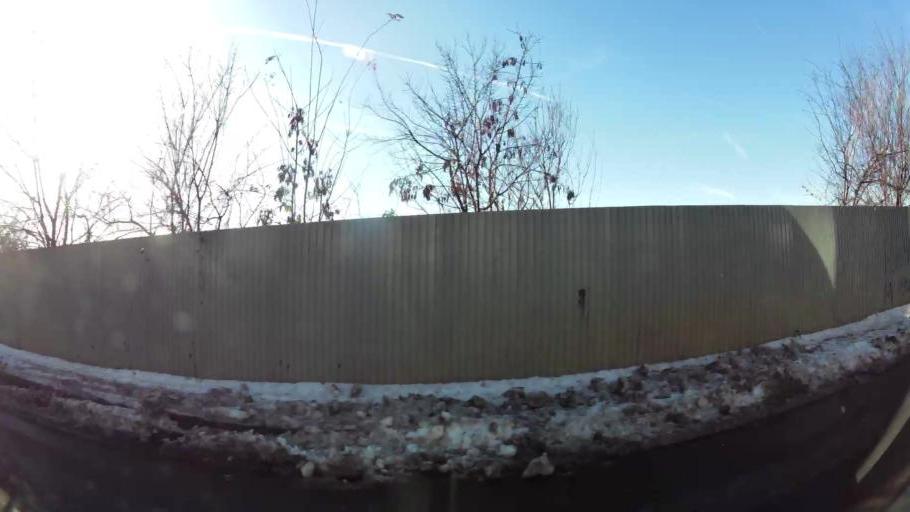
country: RO
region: Ilfov
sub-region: Comuna Fundeni-Dobroesti
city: Fundeni
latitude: 44.4790
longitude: 26.1433
